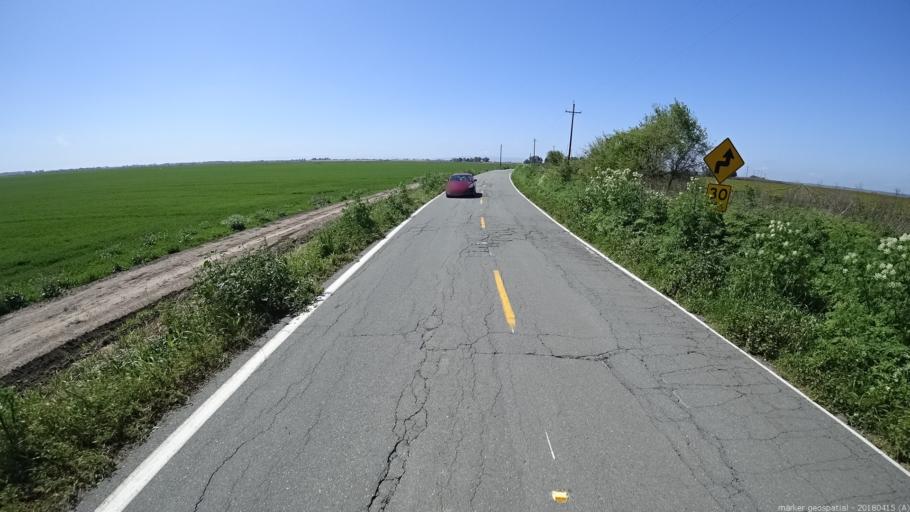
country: US
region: California
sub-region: Solano County
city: Rio Vista
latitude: 38.1466
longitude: -121.6164
